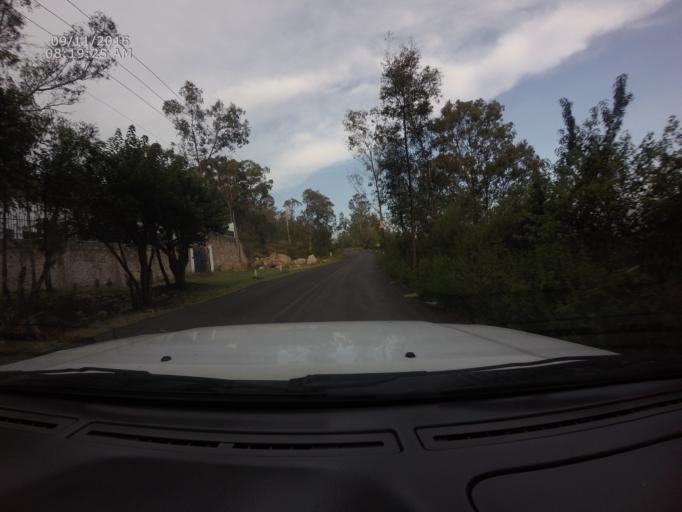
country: MX
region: Michoacan
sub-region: Morelia
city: Morelos
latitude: 19.6359
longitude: -101.2353
